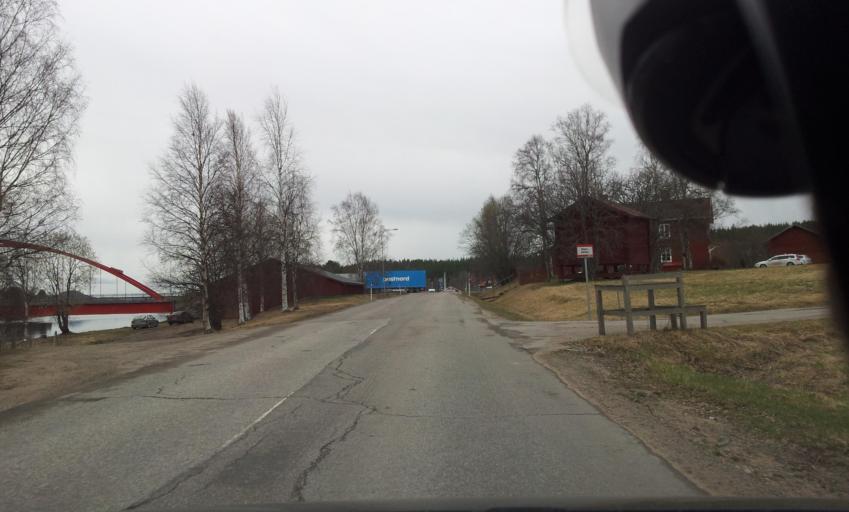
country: SE
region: Gaevleborg
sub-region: Ljusdals Kommun
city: Ljusdal
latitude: 61.8237
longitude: 16.0616
